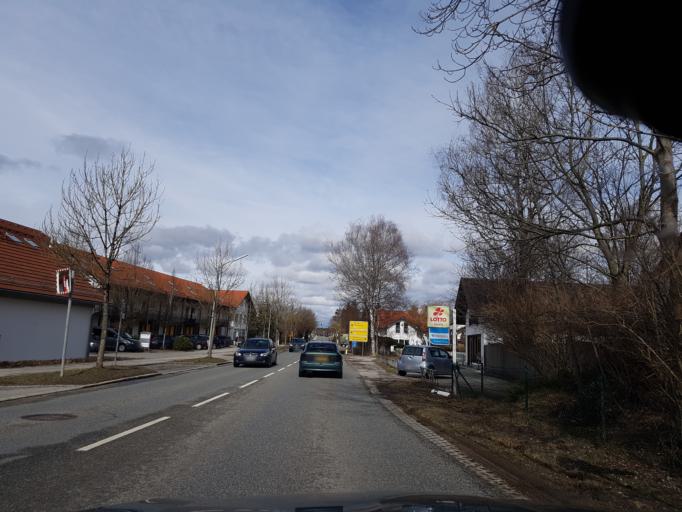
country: DE
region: Bavaria
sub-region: Upper Bavaria
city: Aying
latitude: 47.9422
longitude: 11.7945
